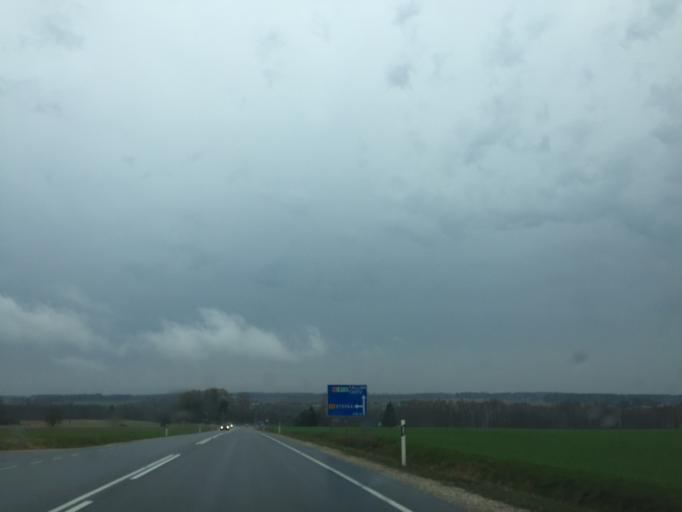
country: EE
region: Tartu
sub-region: UElenurme vald
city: Ulenurme
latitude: 58.2446
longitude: 26.6826
